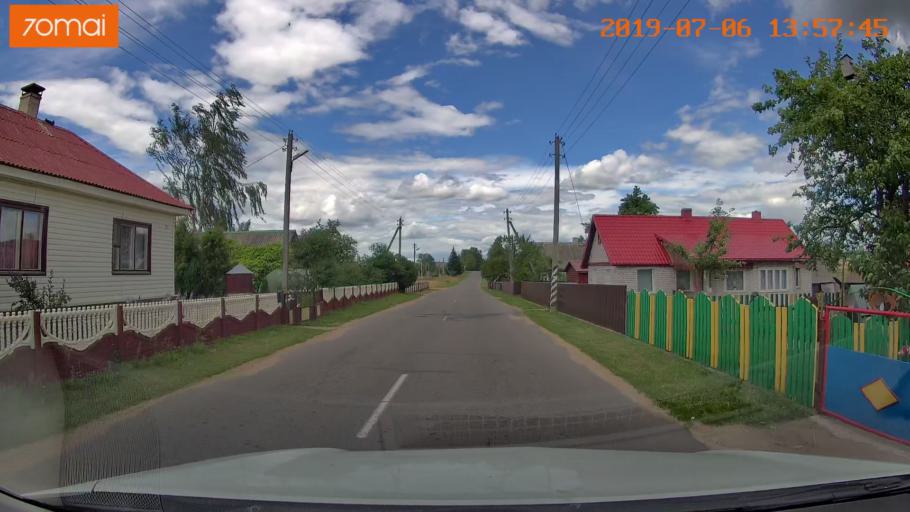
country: BY
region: Minsk
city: Ivyanyets
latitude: 53.7770
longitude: 26.8070
